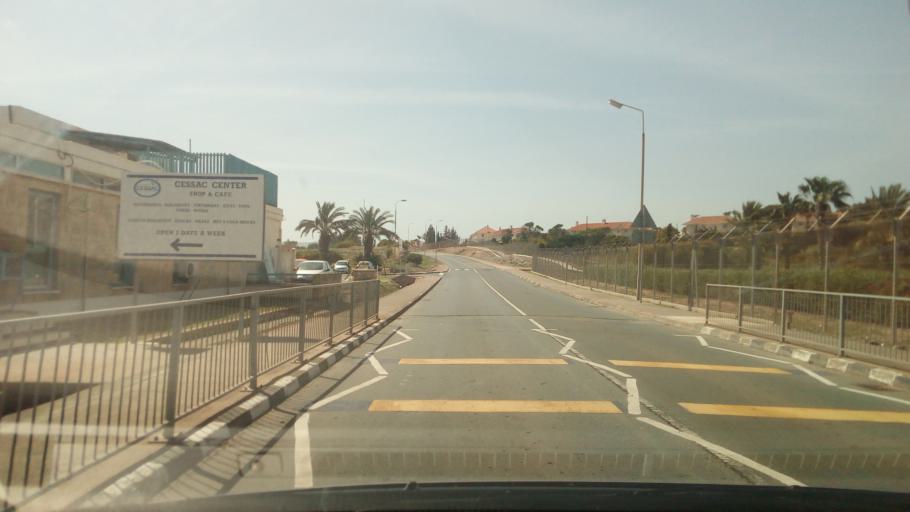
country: CY
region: Larnaka
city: Xylotymbou
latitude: 34.9834
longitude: 33.7344
